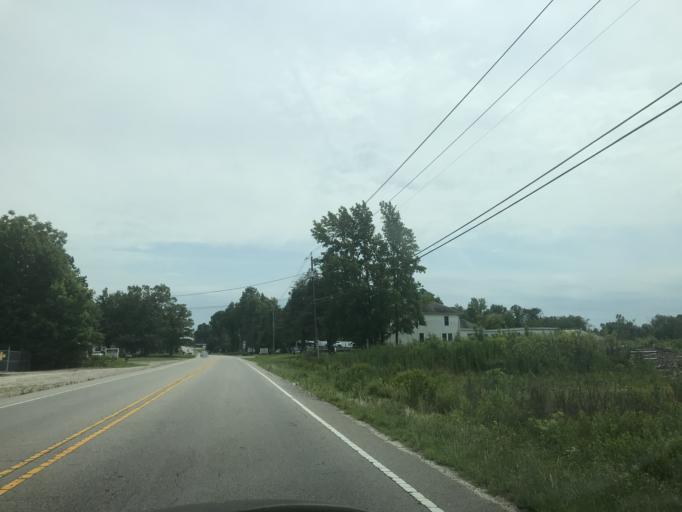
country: US
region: North Carolina
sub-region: Vance County
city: South Henderson
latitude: 36.2832
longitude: -78.4054
